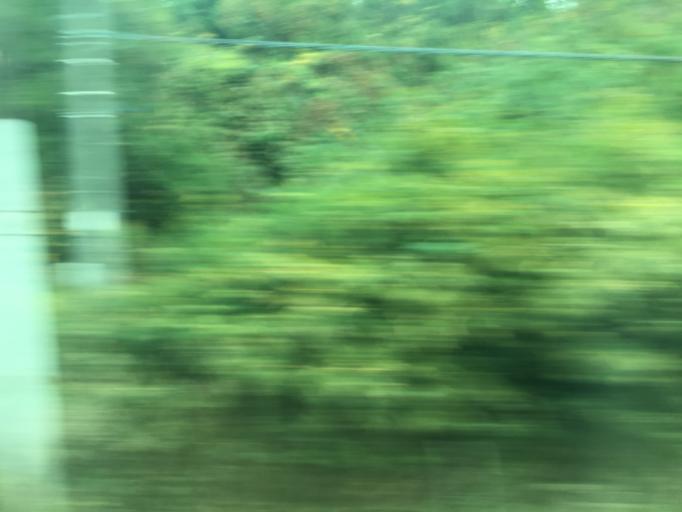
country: JP
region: Ibaraki
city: Ishioka
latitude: 36.1510
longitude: 140.2869
